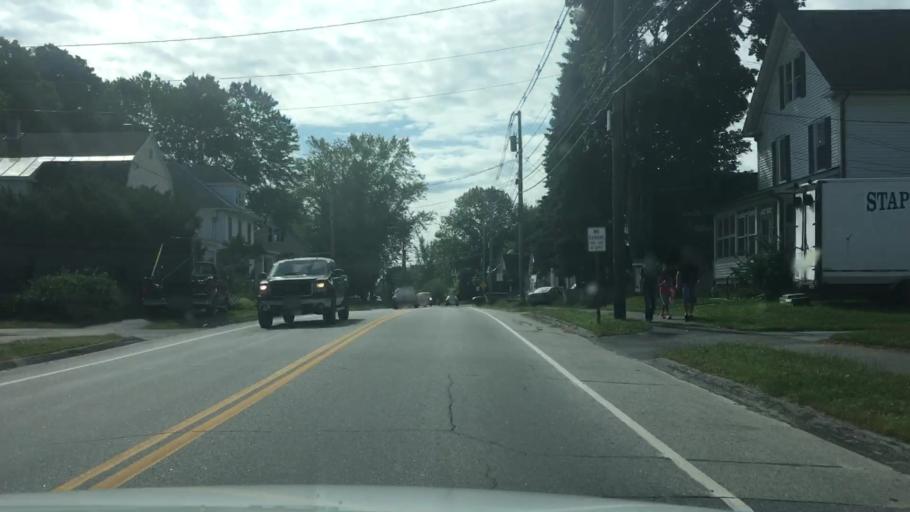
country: US
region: Maine
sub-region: Androscoggin County
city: Auburn
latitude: 44.1087
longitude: -70.2325
